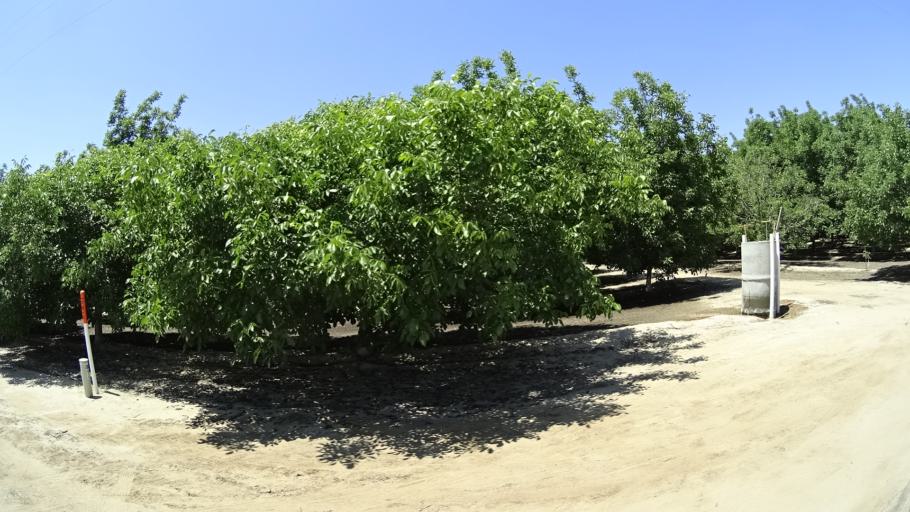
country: US
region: California
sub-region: Fresno County
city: Kingsburg
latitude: 36.4432
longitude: -119.5916
